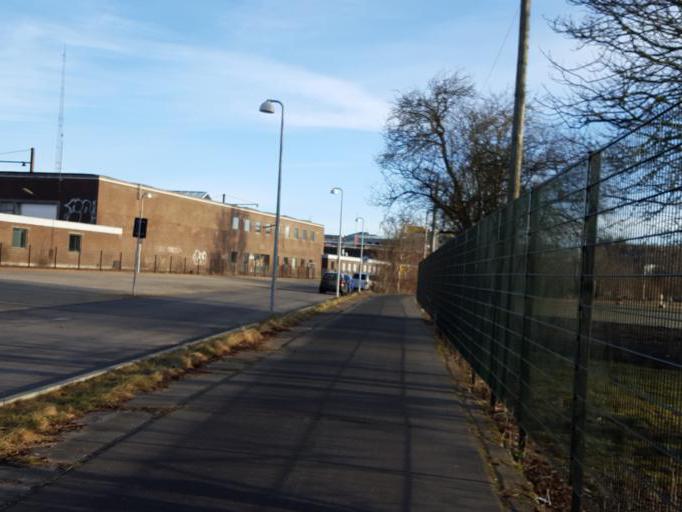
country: DK
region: North Denmark
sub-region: Alborg Kommune
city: Aalborg
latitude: 57.0373
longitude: 9.9184
